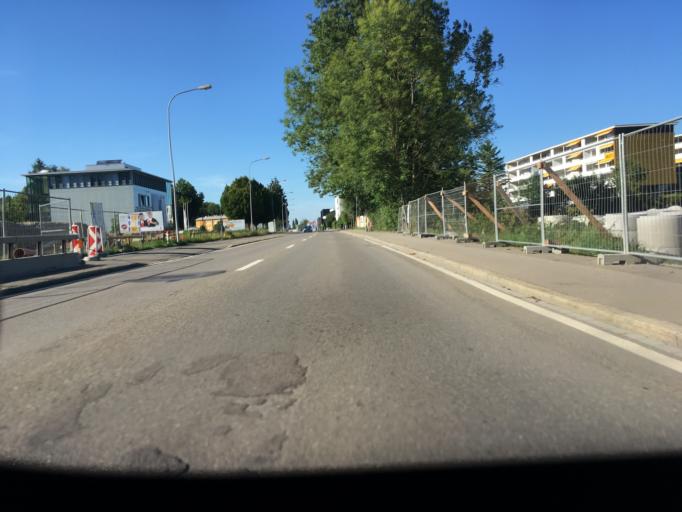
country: CH
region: Zurich
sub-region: Bezirk Horgen
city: Adliswil / Sood
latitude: 47.3232
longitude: 8.5292
